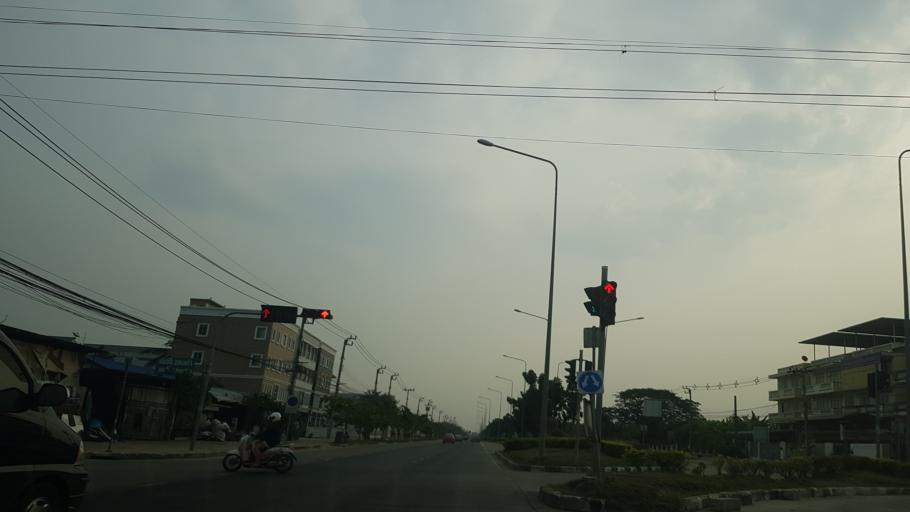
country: TH
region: Bangkok
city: Thawi Watthana
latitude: 13.7656
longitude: 100.3639
